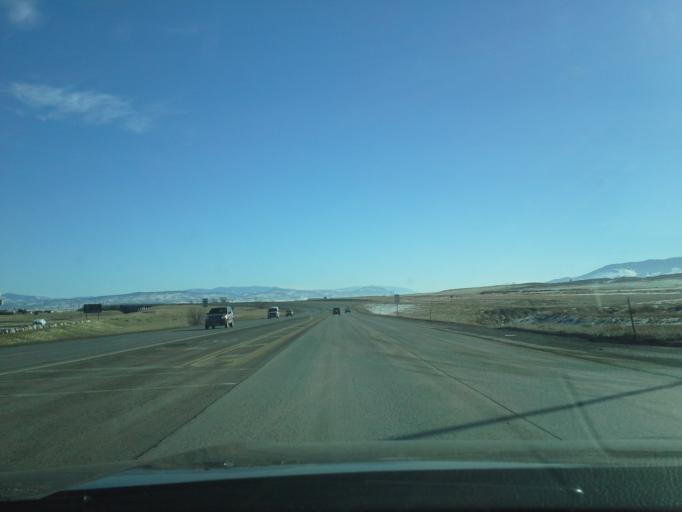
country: US
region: Montana
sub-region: Lewis and Clark County
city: East Helena
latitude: 46.5910
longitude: -111.9566
